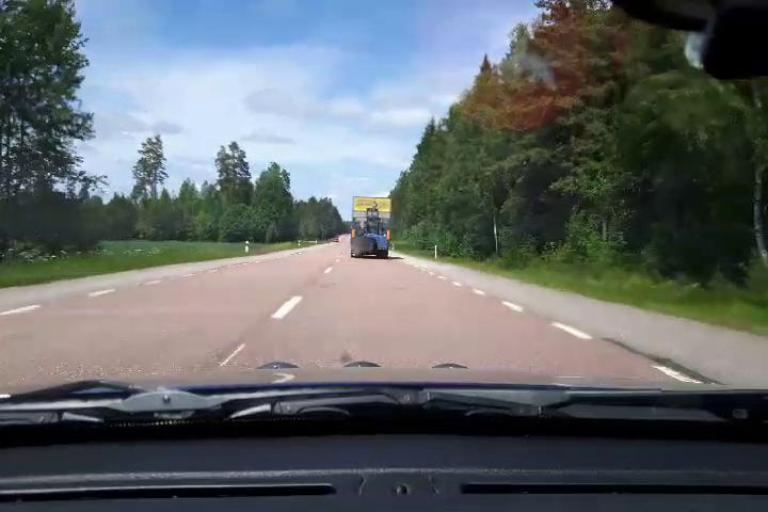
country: SE
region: Uppsala
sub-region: Osthammars Kommun
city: Bjorklinge
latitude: 60.1336
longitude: 17.5083
